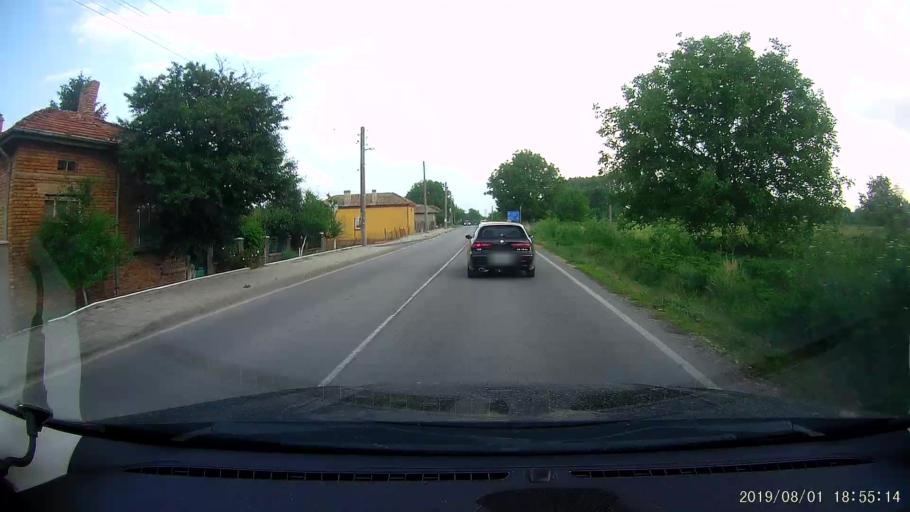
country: BG
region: Shumen
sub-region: Obshtina Smyadovo
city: Smyadovo
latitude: 43.1838
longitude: 27.0048
